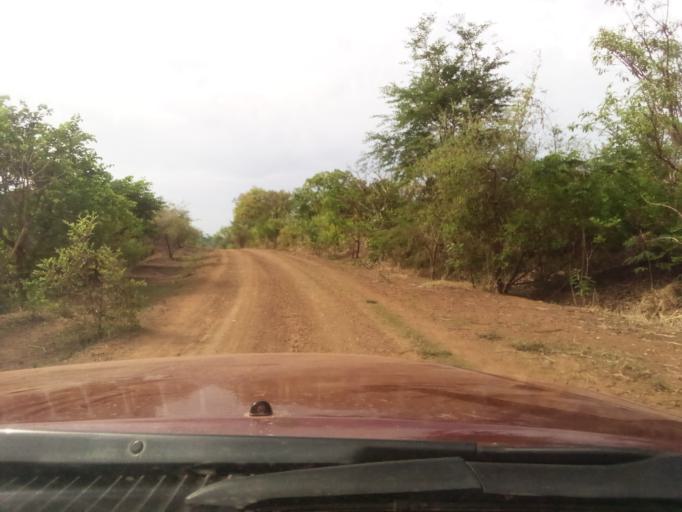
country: ET
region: Oromiya
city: Mendi
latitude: 10.0416
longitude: 35.3065
